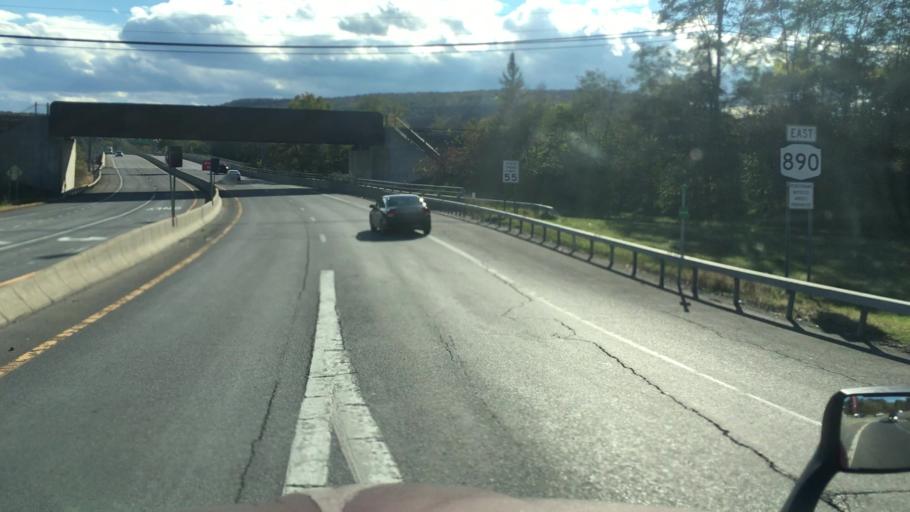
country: US
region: New York
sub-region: Schenectady County
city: Scotia
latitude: 42.8525
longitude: -74.0048
